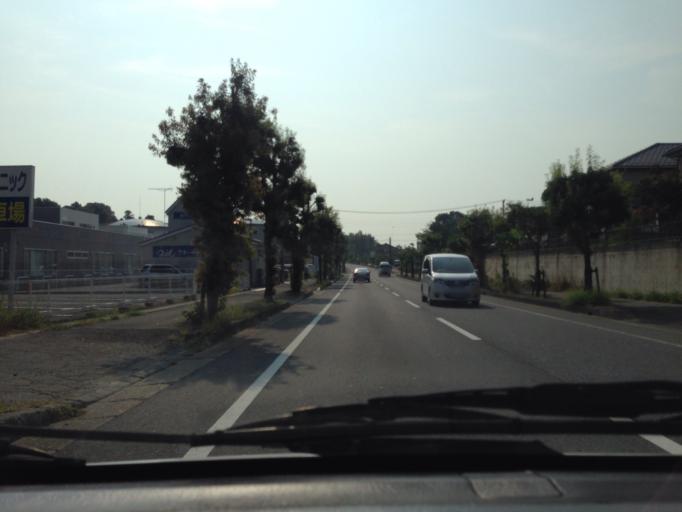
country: JP
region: Ibaraki
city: Ami
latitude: 36.0596
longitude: 140.2049
